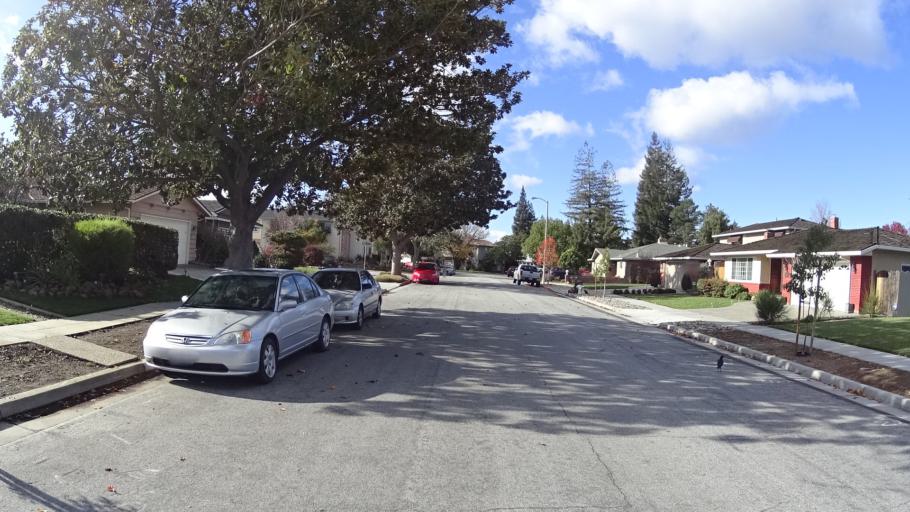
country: US
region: California
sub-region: Santa Clara County
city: Sunnyvale
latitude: 37.3762
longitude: -122.0532
